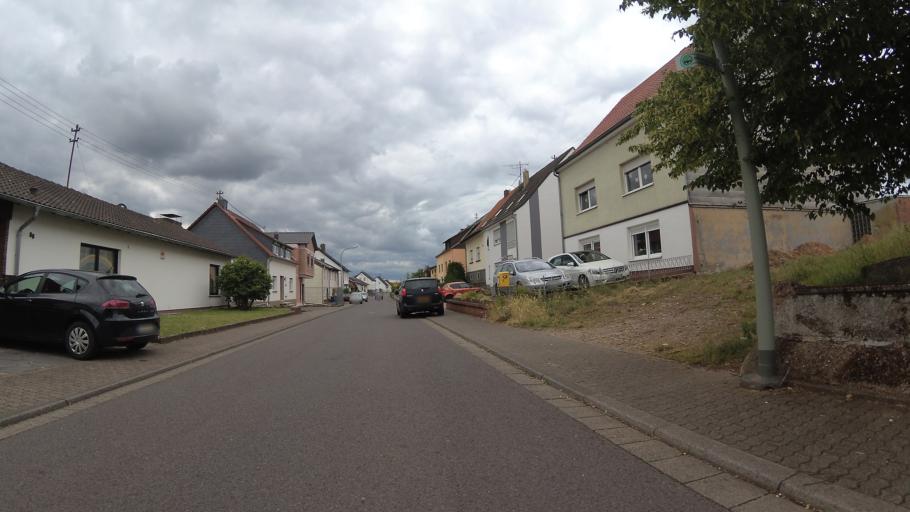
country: DE
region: Saarland
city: Nalbach
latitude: 49.3858
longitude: 6.7969
